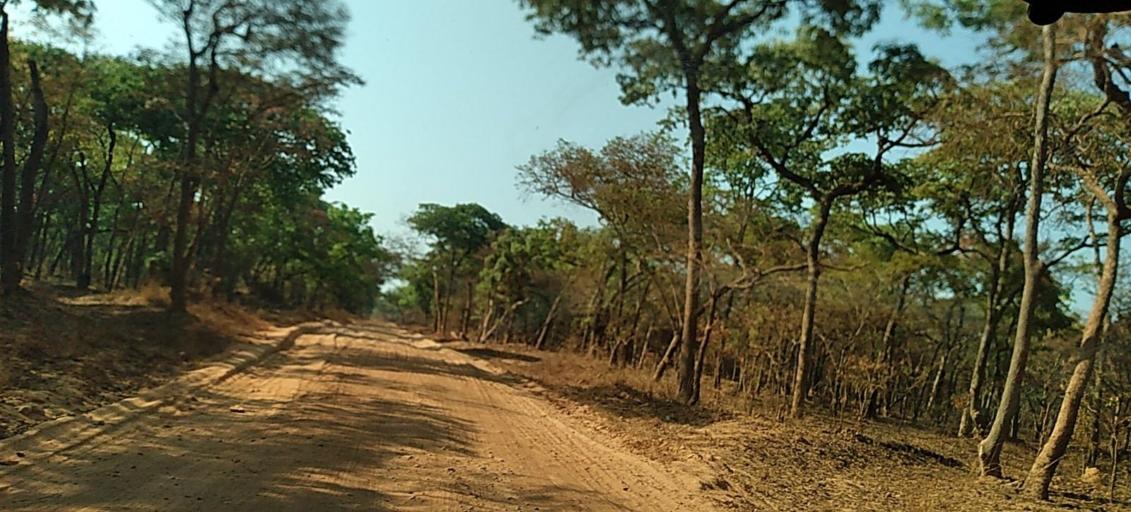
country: ZM
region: North-Western
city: Kasempa
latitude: -13.6777
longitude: 26.0215
